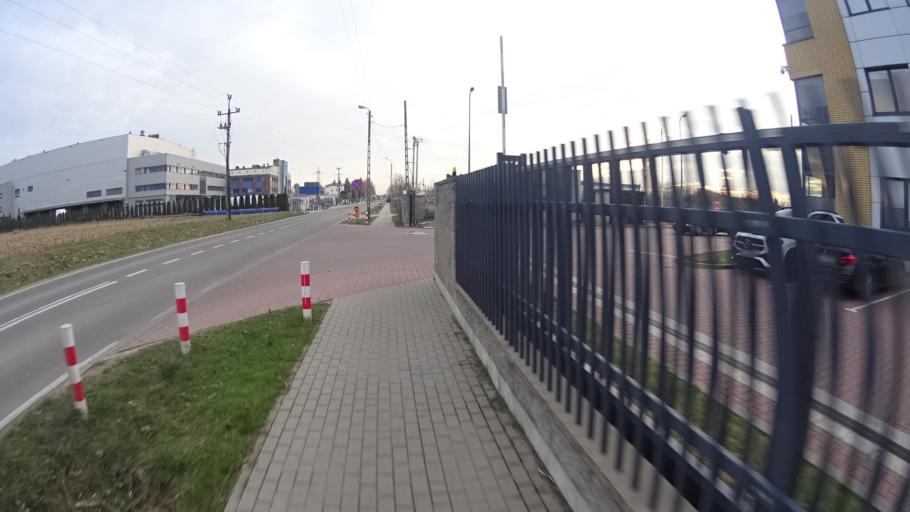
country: PL
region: Masovian Voivodeship
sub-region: Powiat warszawski zachodni
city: Babice
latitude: 52.2189
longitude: 20.8598
